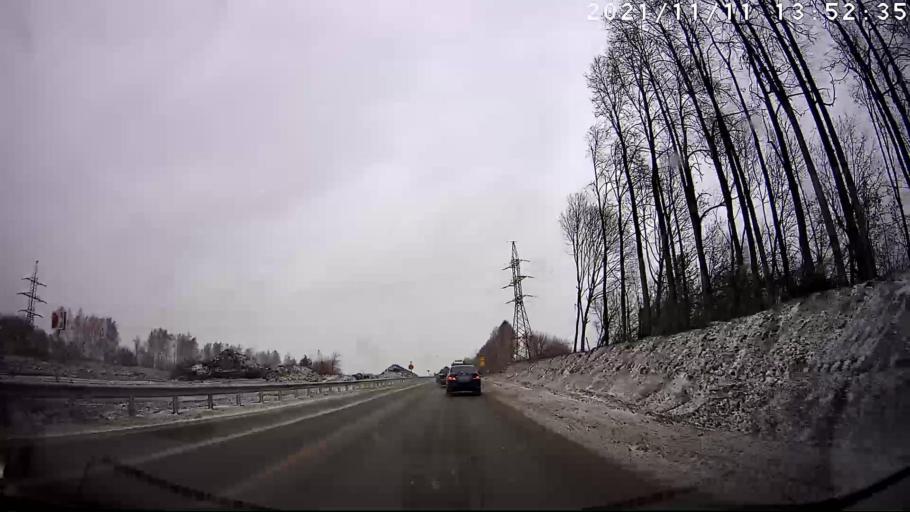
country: RU
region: Chuvashia
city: Shikhazany
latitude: 55.5715
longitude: 47.4098
